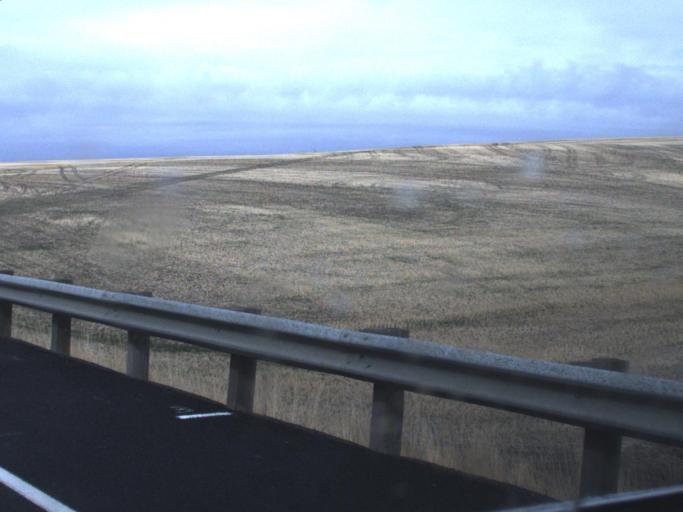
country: US
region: Washington
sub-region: Whitman County
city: Pullman
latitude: 46.5880
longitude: -117.1660
